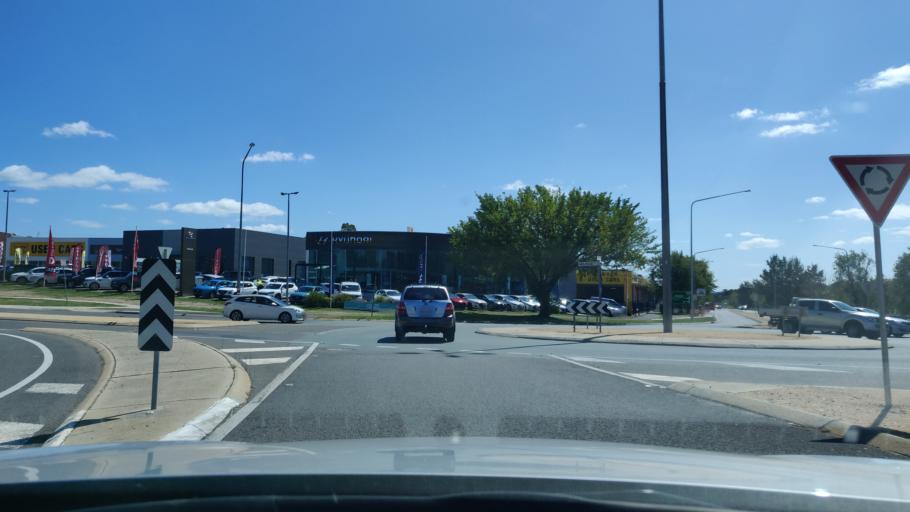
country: AU
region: Australian Capital Territory
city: Forrest
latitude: -35.3575
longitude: 149.0915
